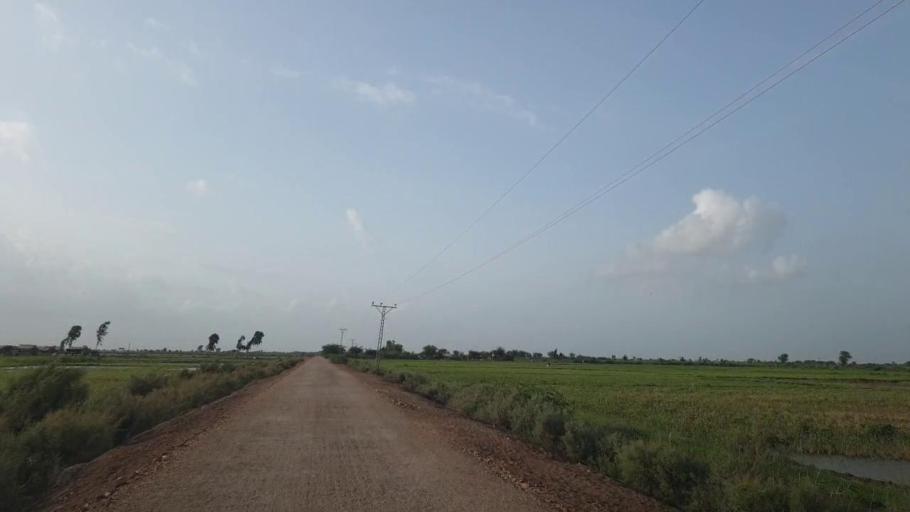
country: PK
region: Sindh
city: Tando Bago
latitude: 24.6570
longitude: 69.1119
